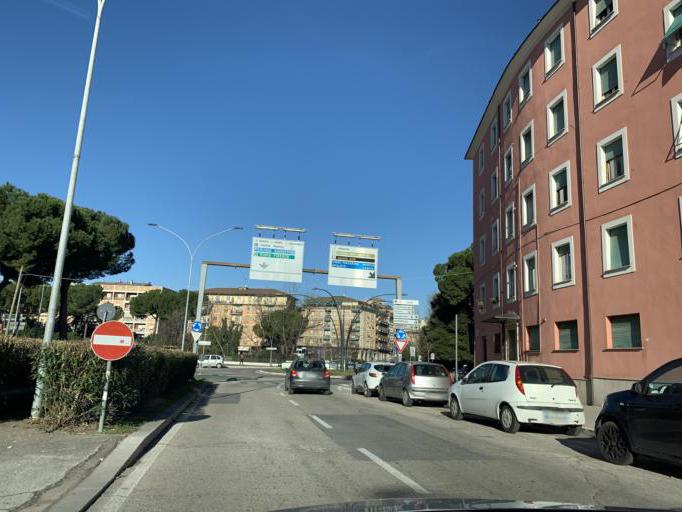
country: IT
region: Umbria
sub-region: Provincia di Terni
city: Terni
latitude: 42.5601
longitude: 12.6524
